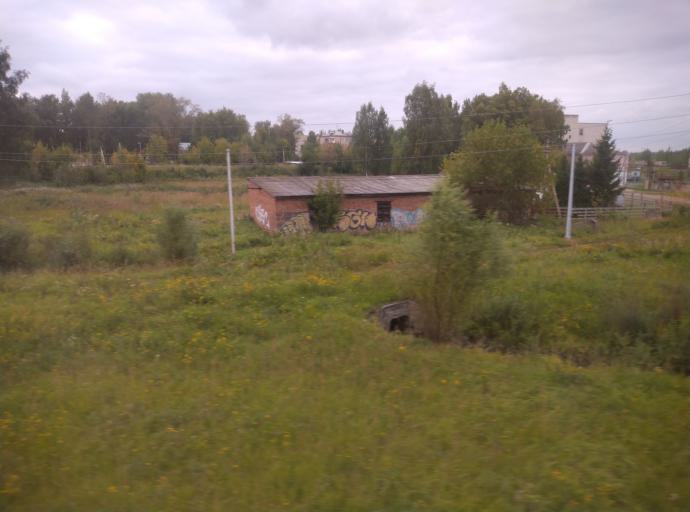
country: RU
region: Kostroma
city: Nerekhta
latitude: 57.4663
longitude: 40.5594
